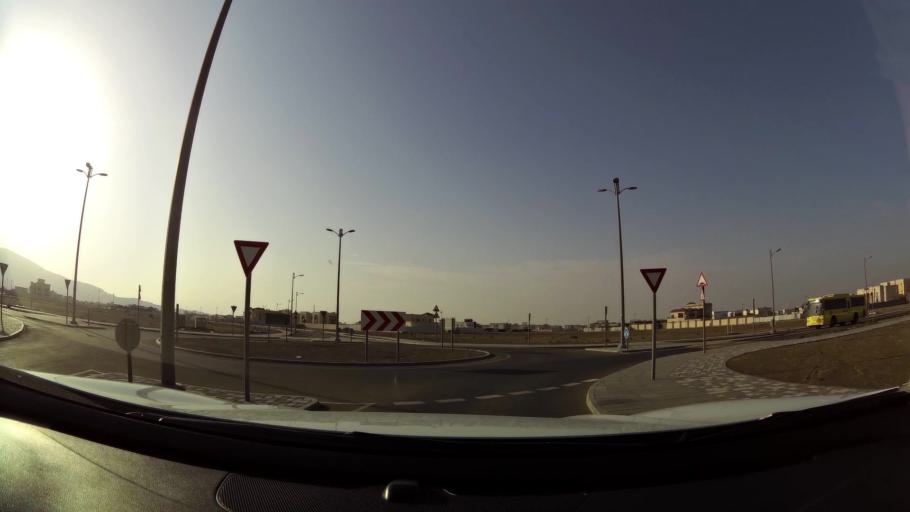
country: AE
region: Abu Dhabi
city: Al Ain
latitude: 24.1031
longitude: 55.8461
